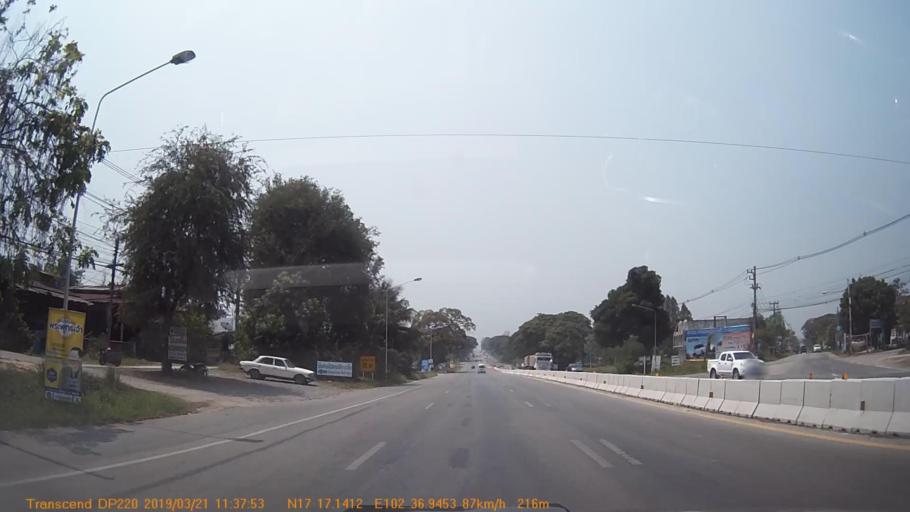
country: TH
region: Changwat Udon Thani
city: Nong Wua So
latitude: 17.2854
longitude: 102.6155
